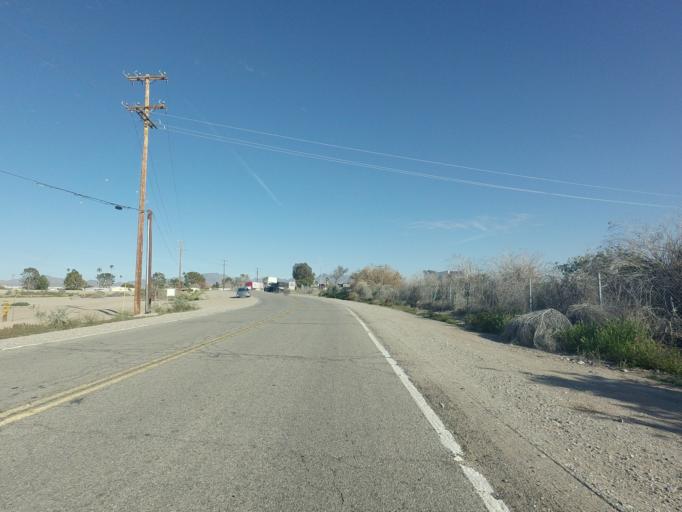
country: US
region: Arizona
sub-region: La Paz County
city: Ehrenberg
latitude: 33.6069
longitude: -114.5385
